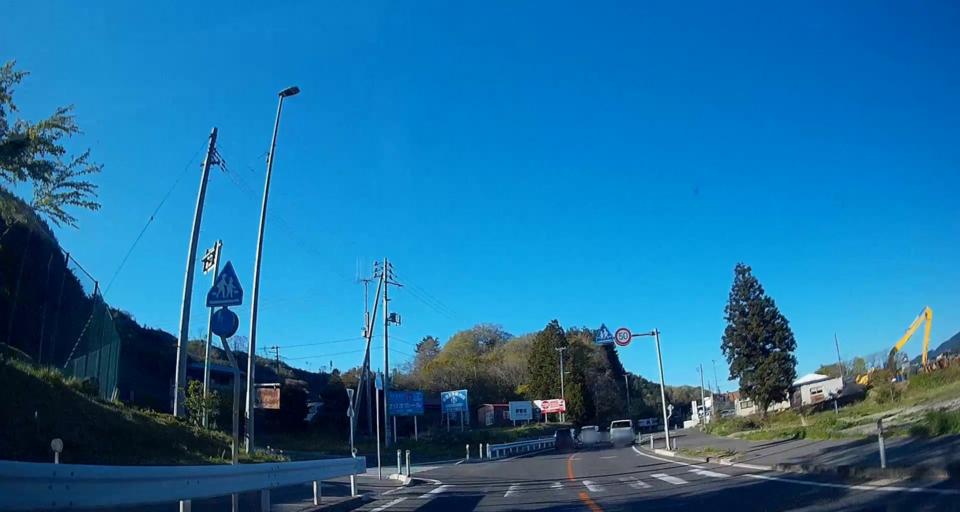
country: JP
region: Iwate
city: Miyako
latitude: 39.5990
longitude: 141.9450
